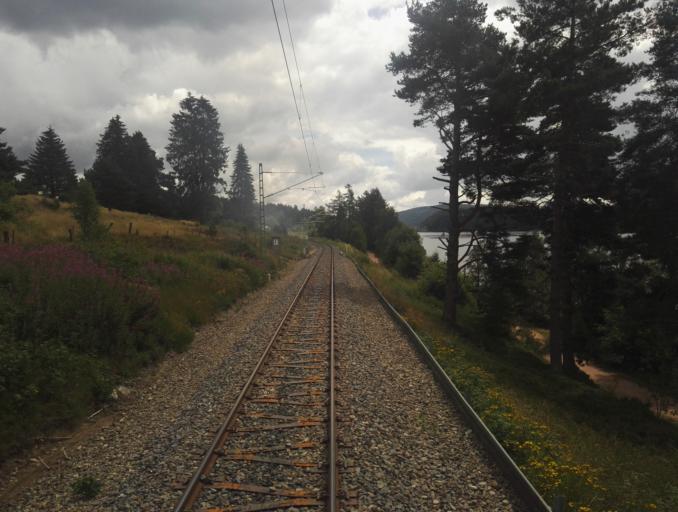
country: DE
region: Baden-Wuerttemberg
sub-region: Freiburg Region
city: Schluchsee
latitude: 47.8229
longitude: 8.1550
